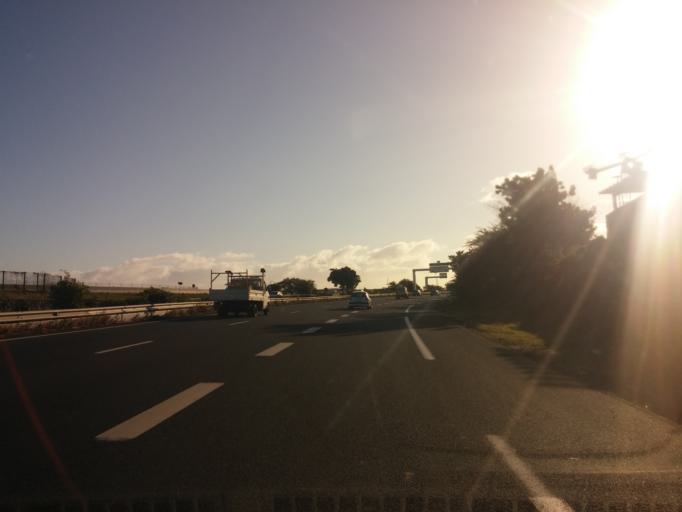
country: RE
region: Reunion
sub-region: Reunion
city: La Possession
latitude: -20.9286
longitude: 55.3319
